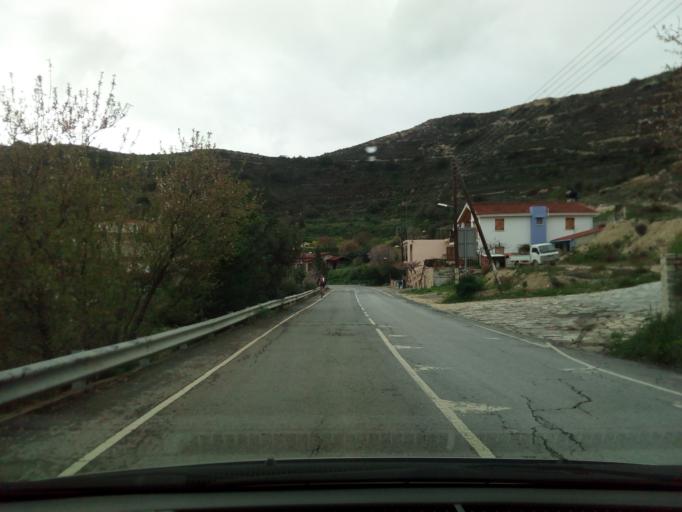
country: CY
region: Lefkosia
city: Lythrodontas
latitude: 34.8629
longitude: 33.3065
